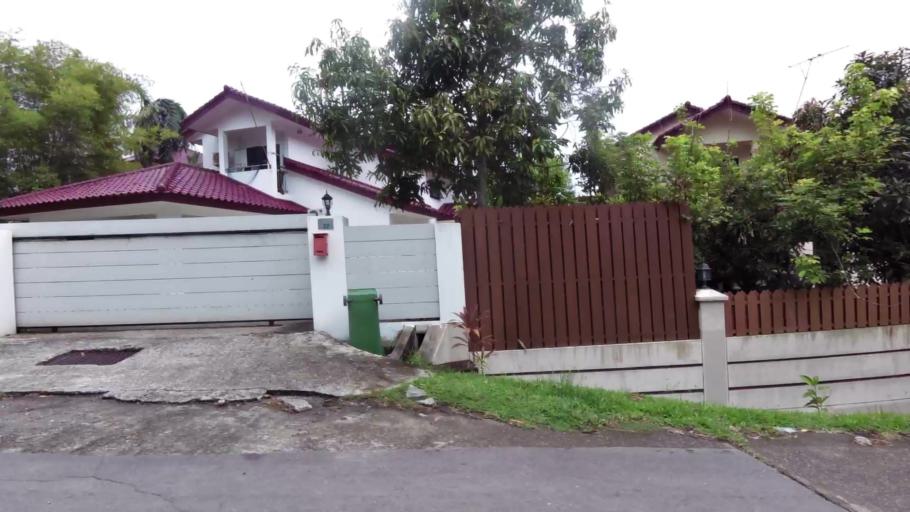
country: BN
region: Brunei and Muara
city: Bandar Seri Begawan
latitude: 4.8870
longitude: 114.9249
